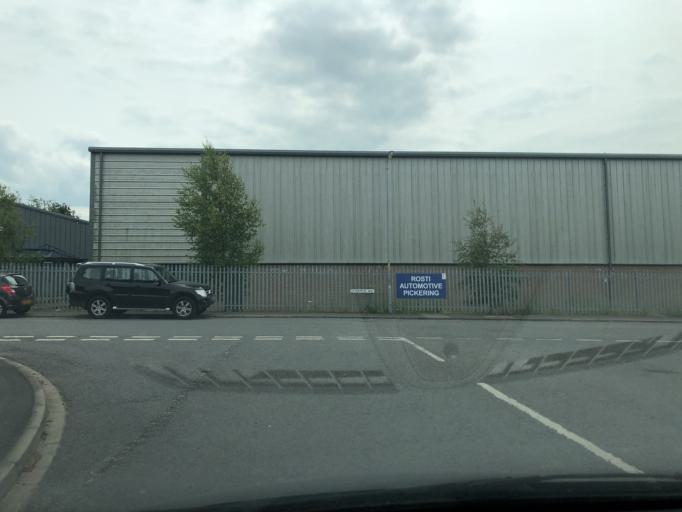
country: GB
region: England
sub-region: North Yorkshire
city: Pickering
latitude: 54.2370
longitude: -0.7599
